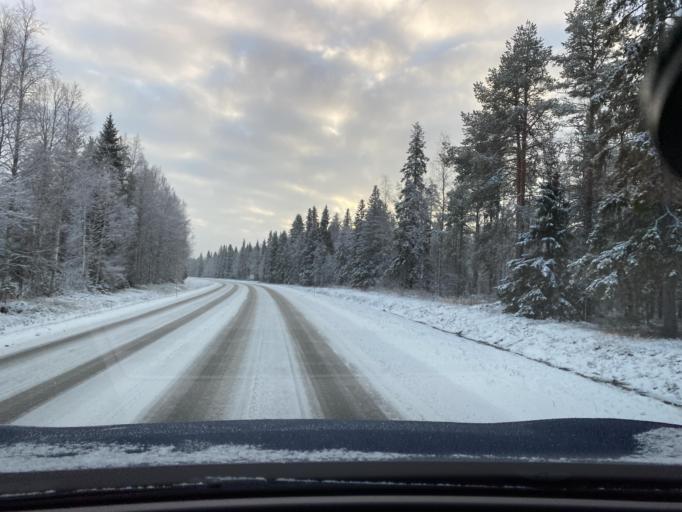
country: FI
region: Lapland
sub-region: Rovaniemi
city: Ranua
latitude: 65.9062
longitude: 26.5185
